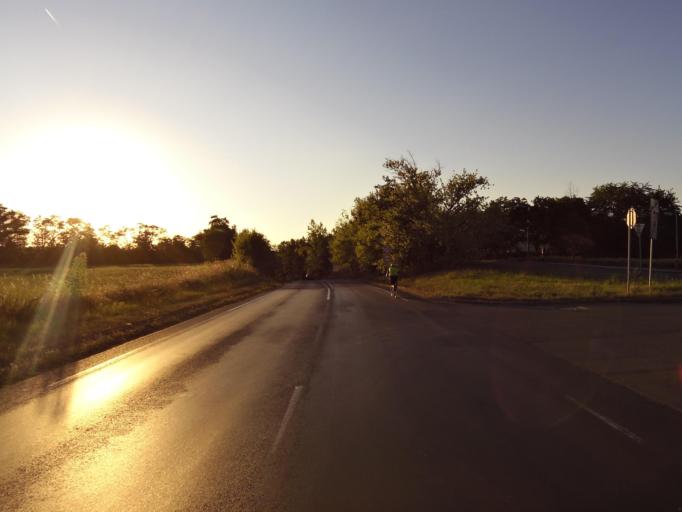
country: CZ
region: Central Bohemia
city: Mnichovo Hradiste
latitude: 50.5175
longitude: 14.9623
